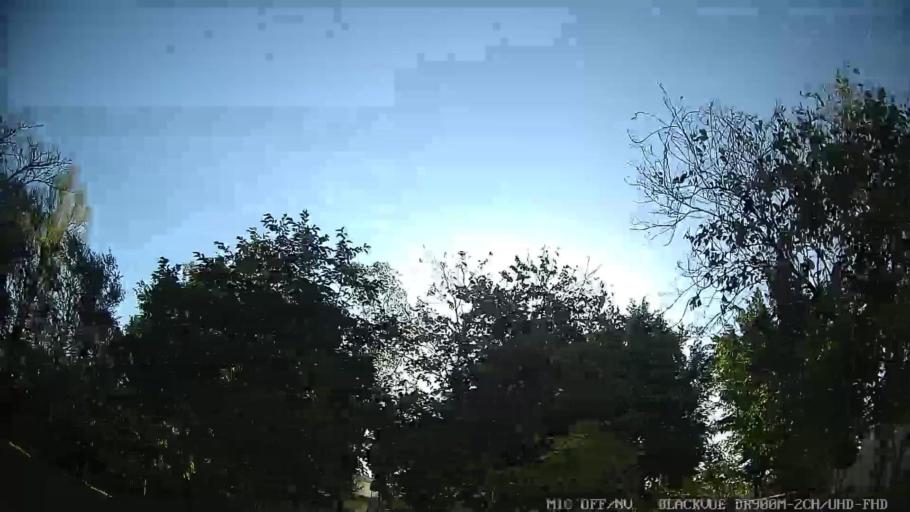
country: BR
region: Sao Paulo
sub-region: Guarulhos
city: Guarulhos
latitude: -23.5406
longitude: -46.5087
